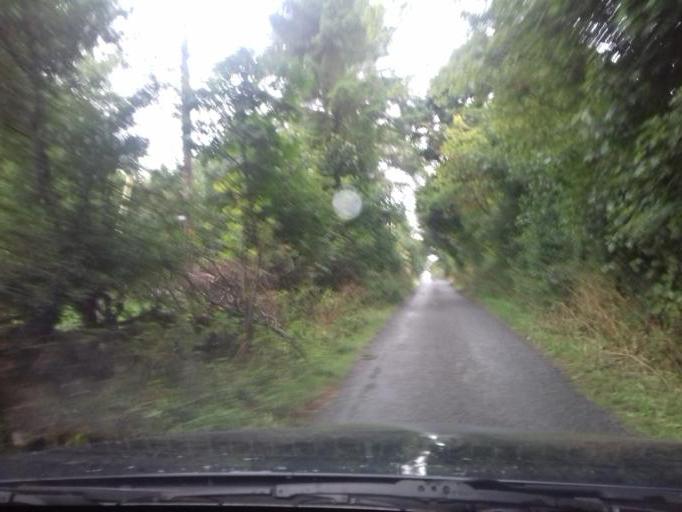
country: IE
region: Leinster
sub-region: Kilkenny
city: Graiguenamanagh
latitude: 52.5736
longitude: -6.9295
